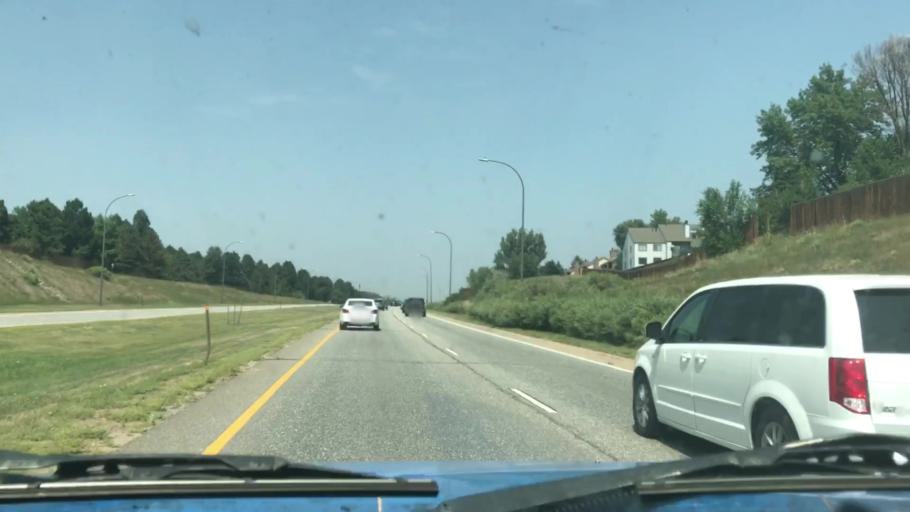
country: US
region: Colorado
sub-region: Jefferson County
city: Lakewood
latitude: 39.6755
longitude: -105.1194
